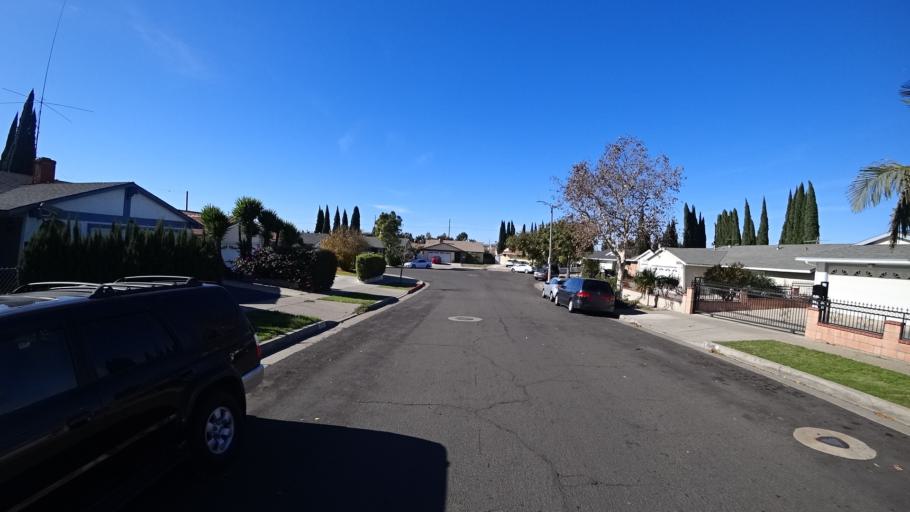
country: US
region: California
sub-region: Orange County
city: Garden Grove
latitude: 33.7557
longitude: -117.9355
